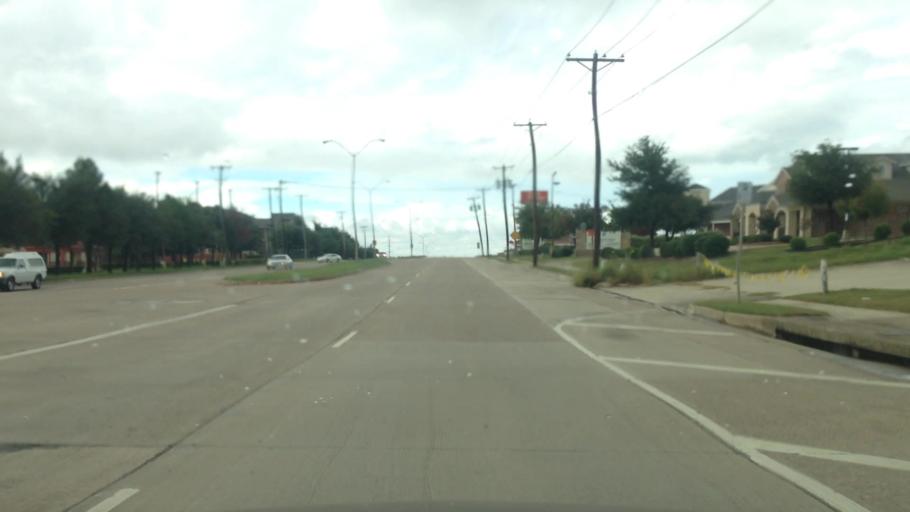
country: US
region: Texas
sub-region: Tarrant County
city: Benbrook
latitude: 32.6447
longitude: -97.4097
